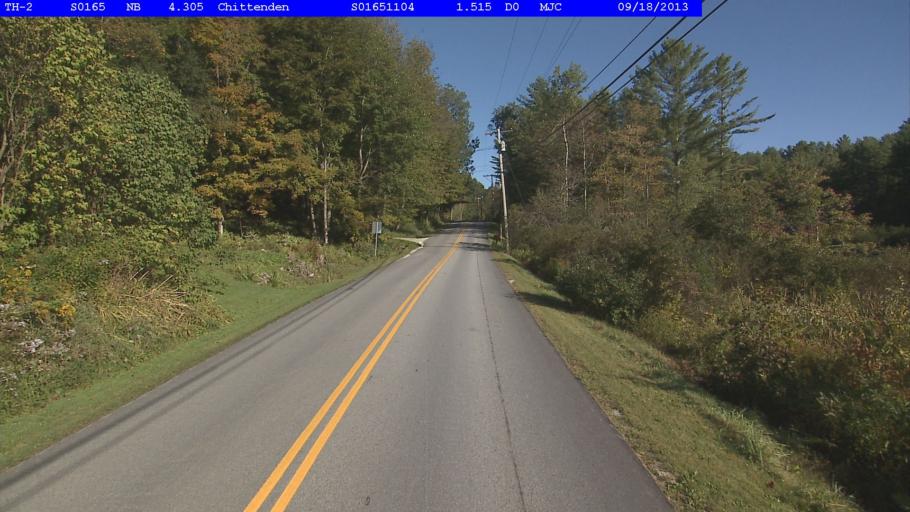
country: US
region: Vermont
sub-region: Rutland County
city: Rutland
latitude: 43.6976
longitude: -72.9580
